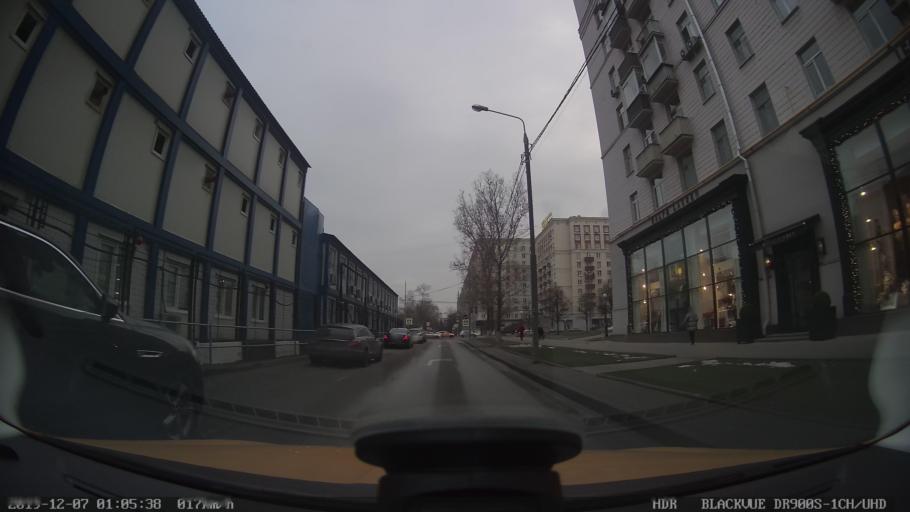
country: RU
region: Moskovskaya
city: Dorogomilovo
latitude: 55.7505
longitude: 37.5629
